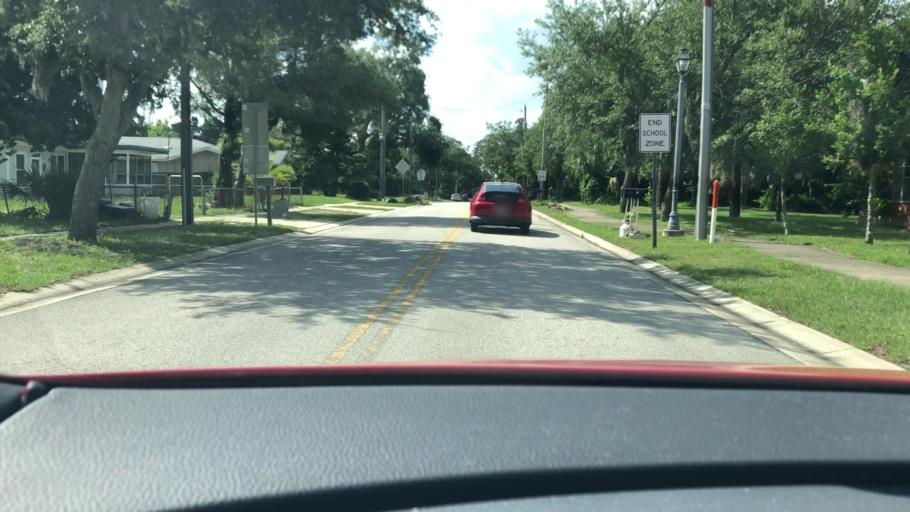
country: US
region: Florida
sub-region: Volusia County
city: Ormond Beach
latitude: 29.2826
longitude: -81.0578
